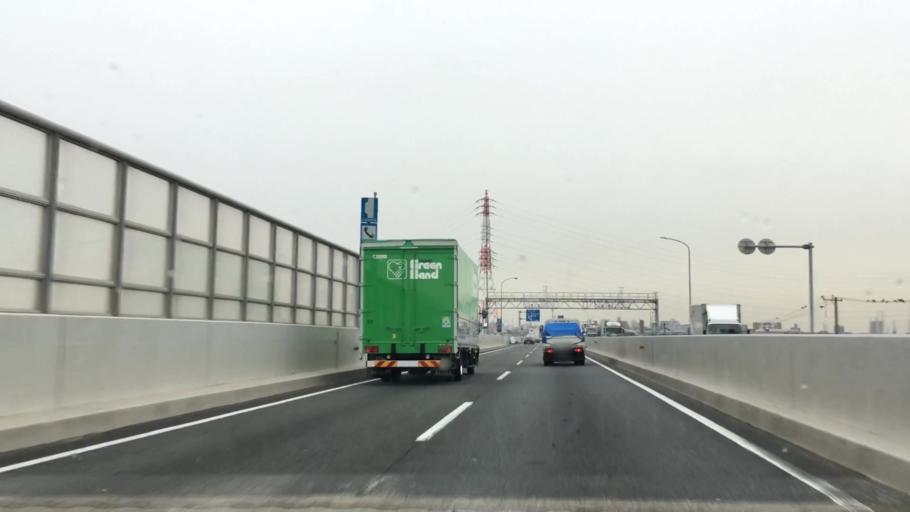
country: JP
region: Aichi
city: Chiryu
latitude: 34.9966
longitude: 137.0319
